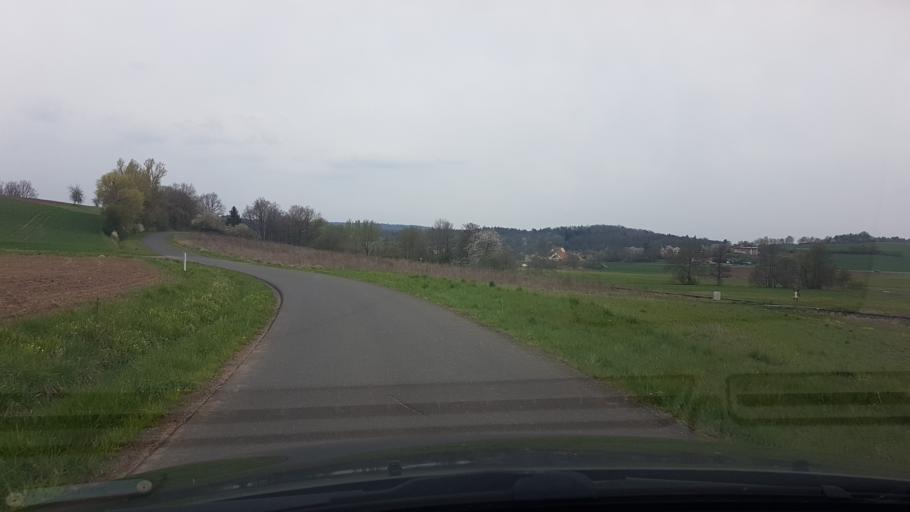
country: DE
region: Bavaria
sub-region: Regierungsbezirk Unterfranken
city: Rentweinsdorf
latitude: 50.0531
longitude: 10.8198
